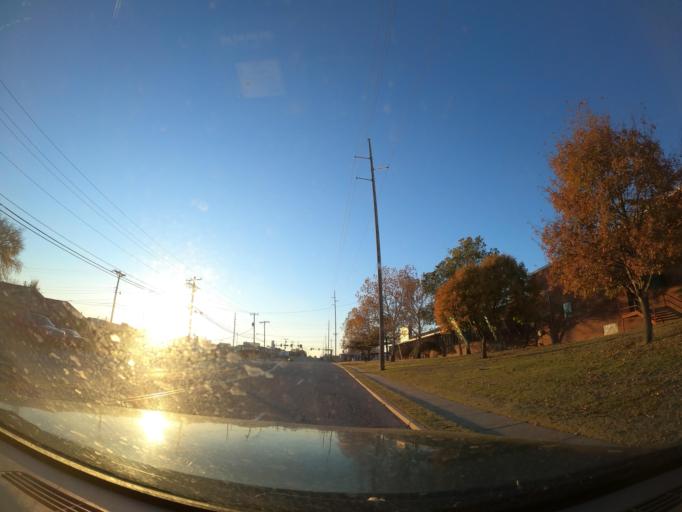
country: US
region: Oklahoma
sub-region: Tulsa County
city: Tulsa
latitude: 36.1408
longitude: -95.9031
